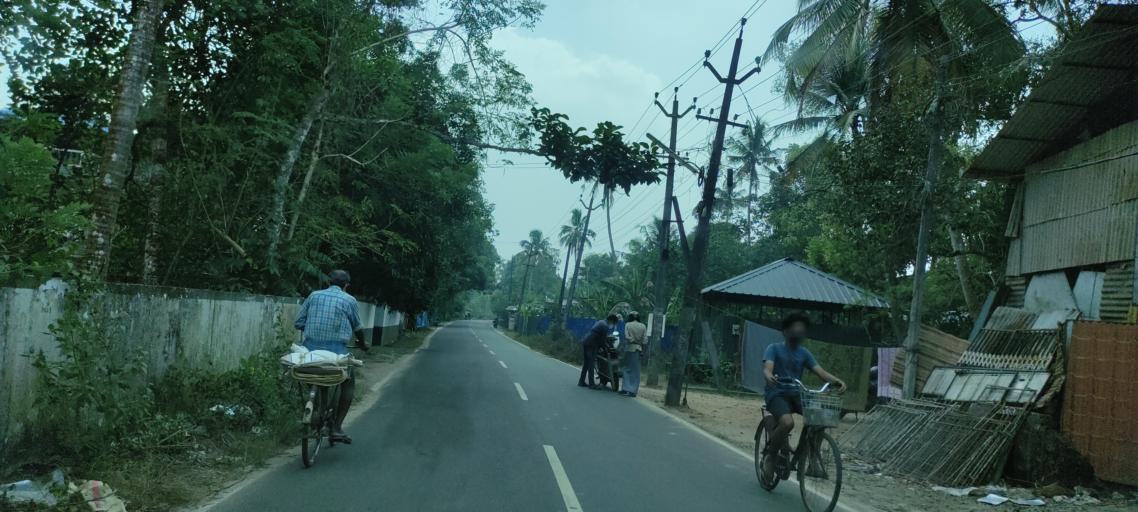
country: IN
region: Kerala
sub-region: Alappuzha
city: Alleppey
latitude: 9.5750
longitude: 76.3393
